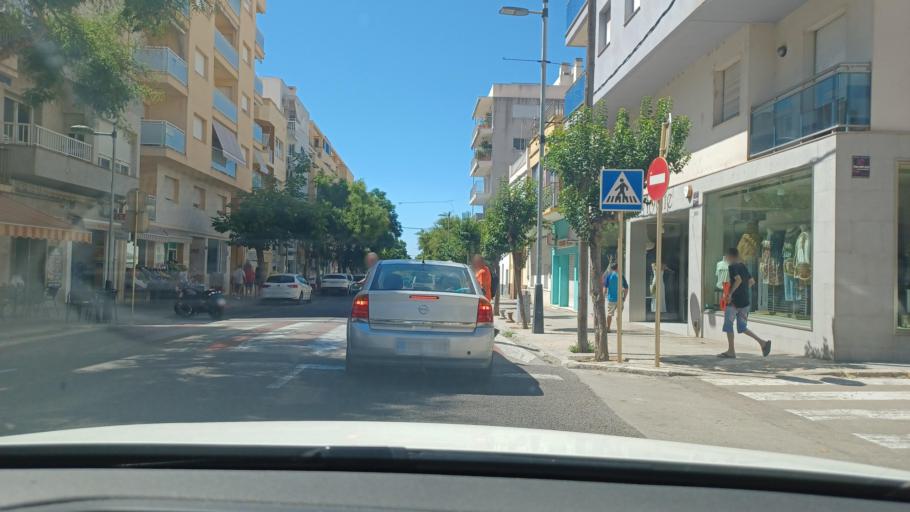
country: ES
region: Catalonia
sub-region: Provincia de Tarragona
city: Sant Carles de la Rapita
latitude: 40.6151
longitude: 0.5877
